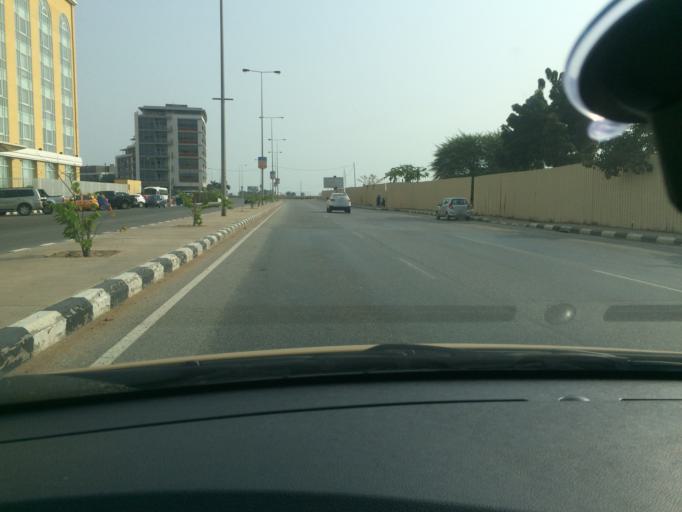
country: AO
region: Luanda
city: Luanda
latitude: -8.8157
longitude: 13.2194
